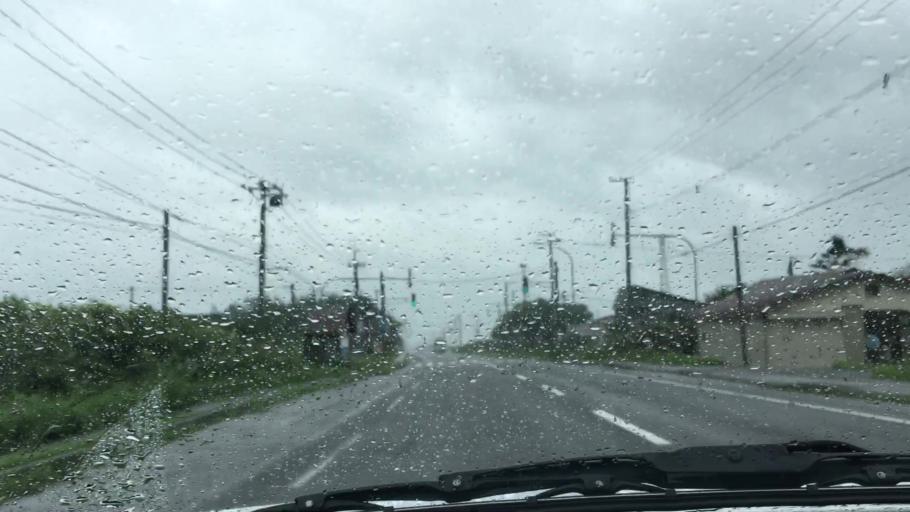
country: JP
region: Hokkaido
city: Nanae
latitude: 42.3151
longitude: 140.2739
